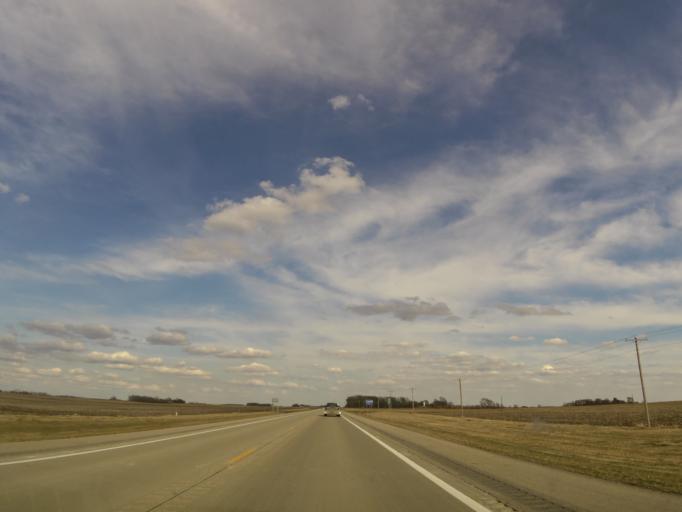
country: US
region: Minnesota
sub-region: Lac qui Parle County
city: Dawson
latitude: 44.9361
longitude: -96.0046
